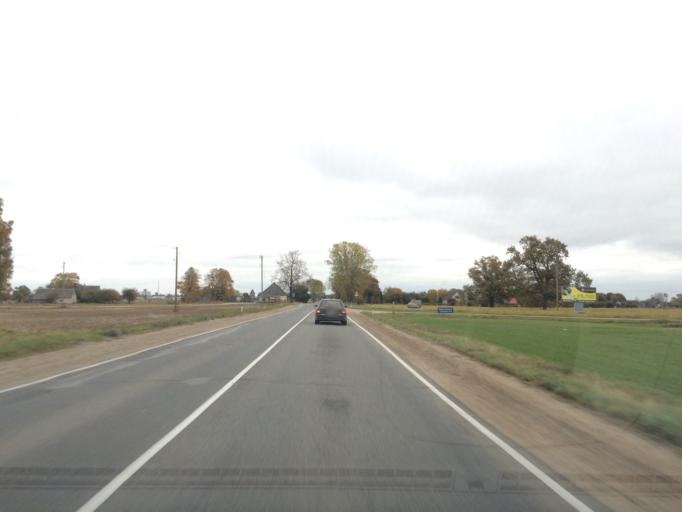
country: LV
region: Jekabpils Rajons
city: Jekabpils
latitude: 56.5290
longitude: 25.8262
